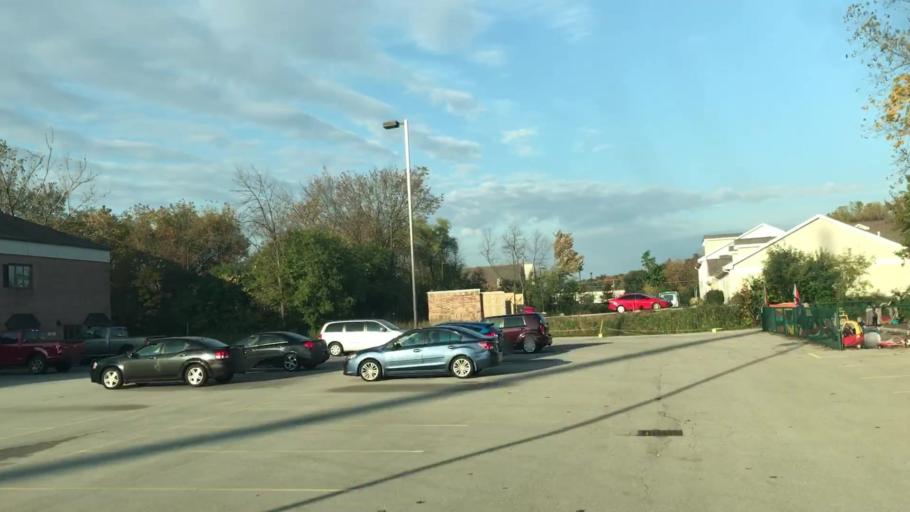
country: US
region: Wisconsin
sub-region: Waukesha County
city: Brookfield
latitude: 43.0383
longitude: -88.1347
